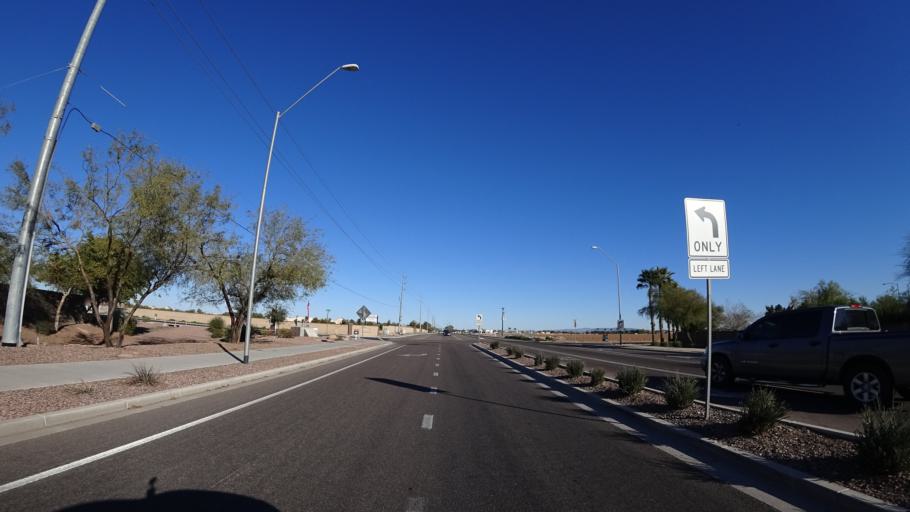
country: US
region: Arizona
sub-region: Maricopa County
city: Goodyear
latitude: 33.4501
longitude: -112.3990
